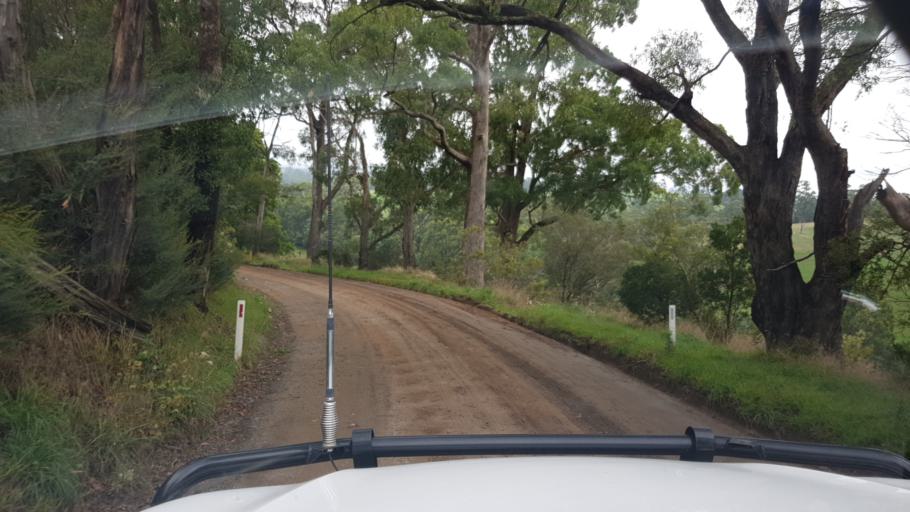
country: AU
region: Victoria
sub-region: Latrobe
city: Moe
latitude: -38.0737
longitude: 146.1456
